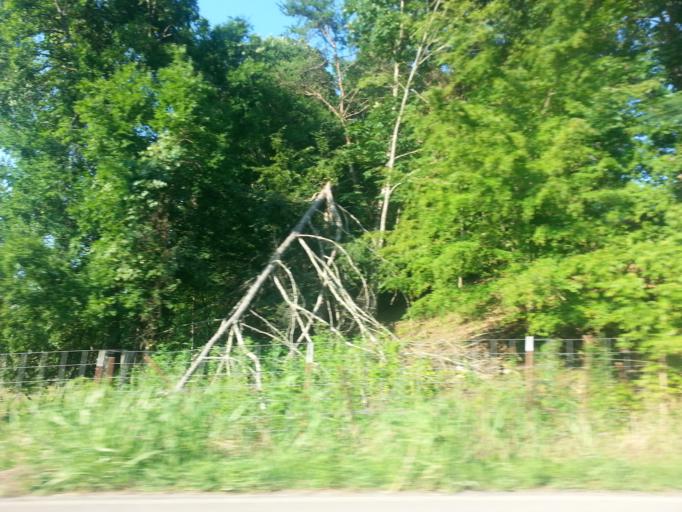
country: US
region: Tennessee
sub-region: Blount County
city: Maryville
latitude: 35.7101
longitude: -83.9120
